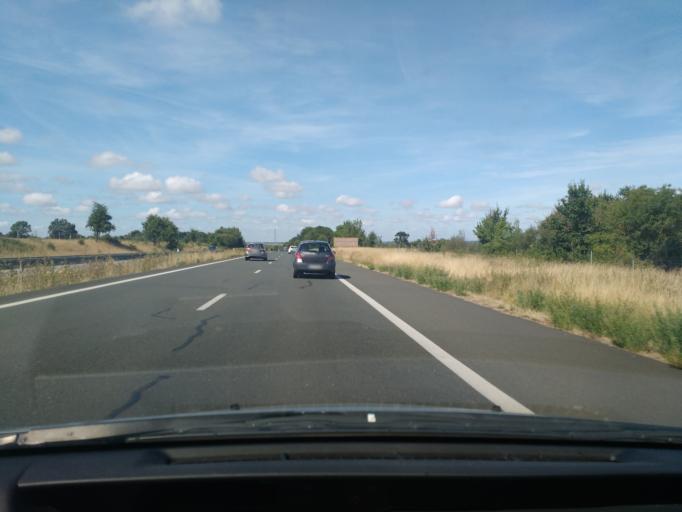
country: FR
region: Pays de la Loire
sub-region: Departement de la Loire-Atlantique
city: Saint-Herblon
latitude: 47.4201
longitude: -1.1102
